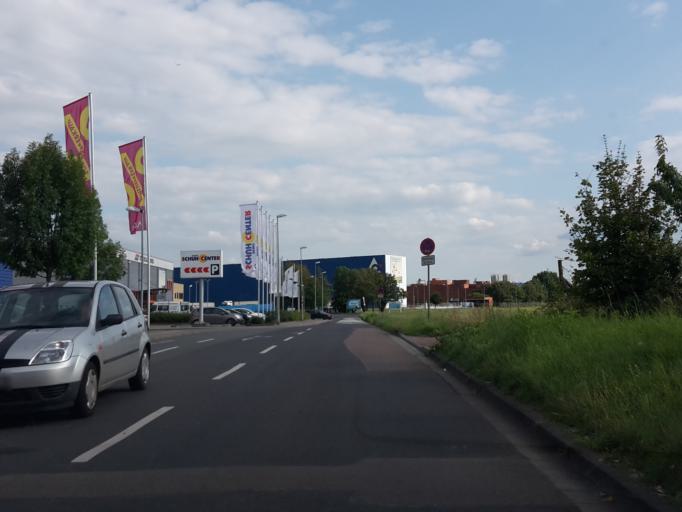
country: DE
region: Hesse
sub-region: Regierungsbezirk Giessen
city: Dehrn
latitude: 50.3975
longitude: 8.0780
